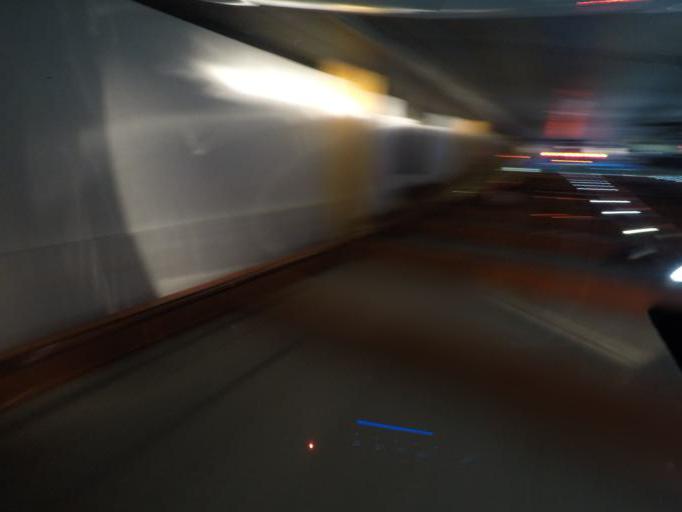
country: BR
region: Goias
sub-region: Goiania
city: Goiania
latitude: -16.7093
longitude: -49.2363
